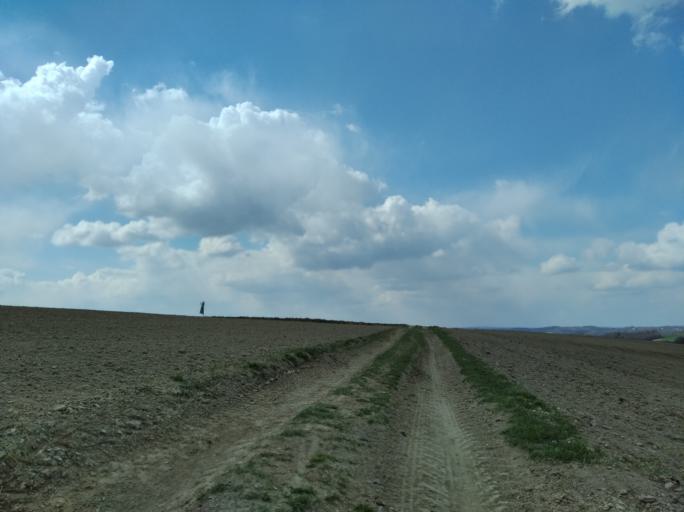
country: PL
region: Subcarpathian Voivodeship
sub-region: Powiat strzyzowski
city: Strzyzow
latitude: 49.9112
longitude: 21.7515
